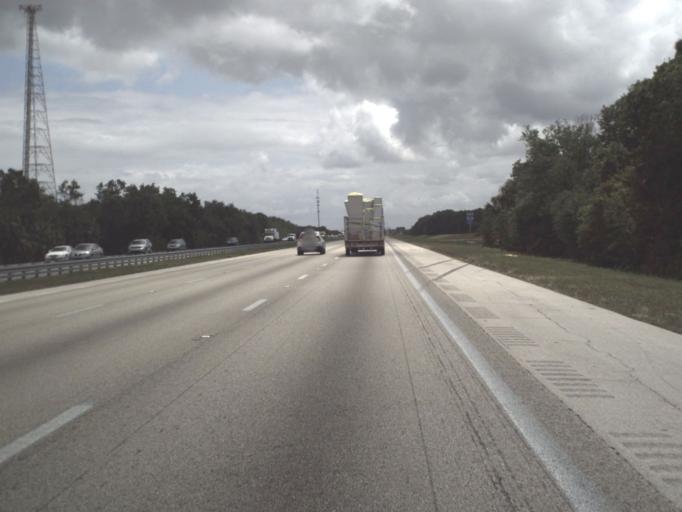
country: US
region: Florida
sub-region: Brevard County
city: South Patrick Shores
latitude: 28.2105
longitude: -80.7129
